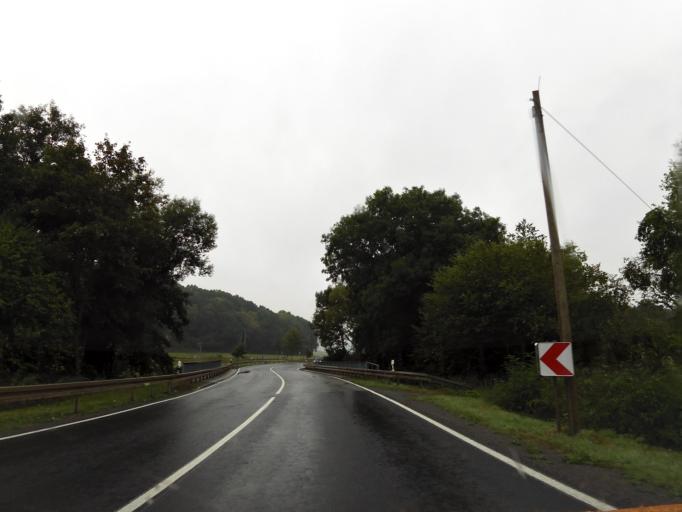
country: DE
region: Thuringia
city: Ilfeld
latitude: 51.5677
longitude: 10.7786
